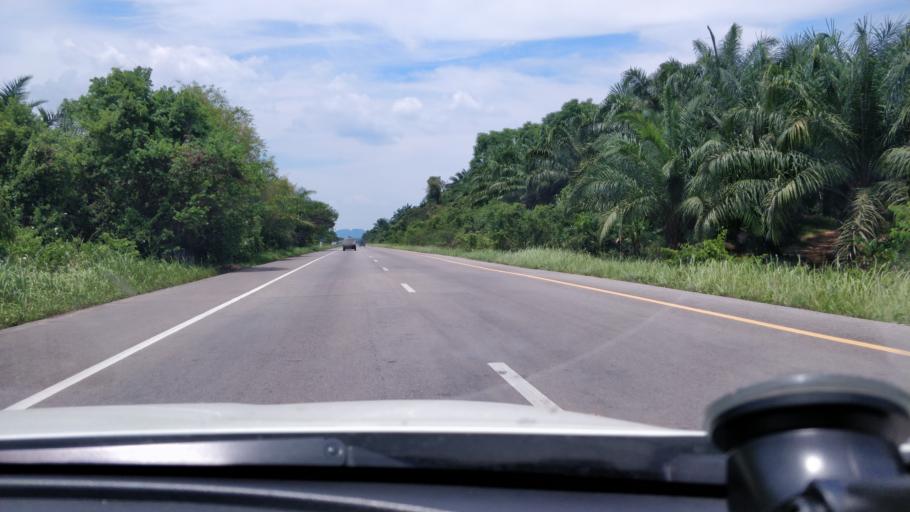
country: TH
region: Krabi
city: Plai Phraya
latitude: 8.5154
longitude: 98.8916
